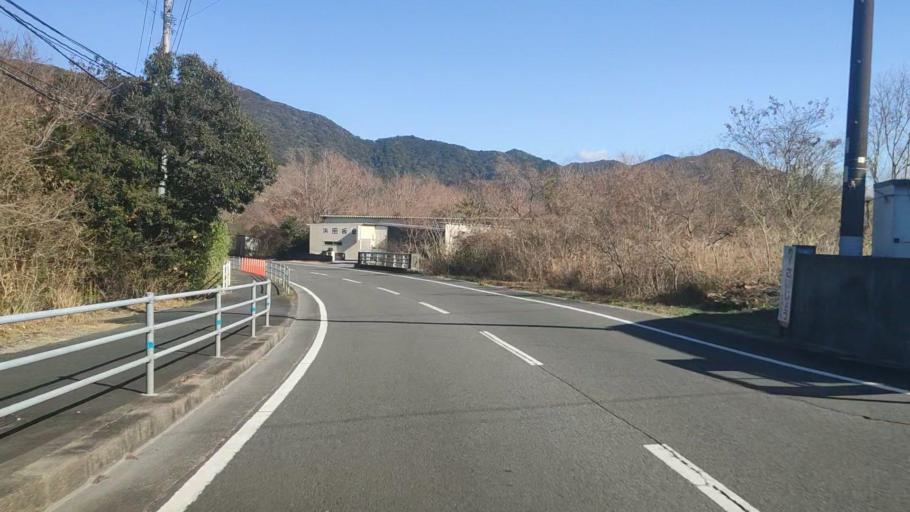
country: JP
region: Oita
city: Saiki
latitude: 32.8011
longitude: 131.9427
